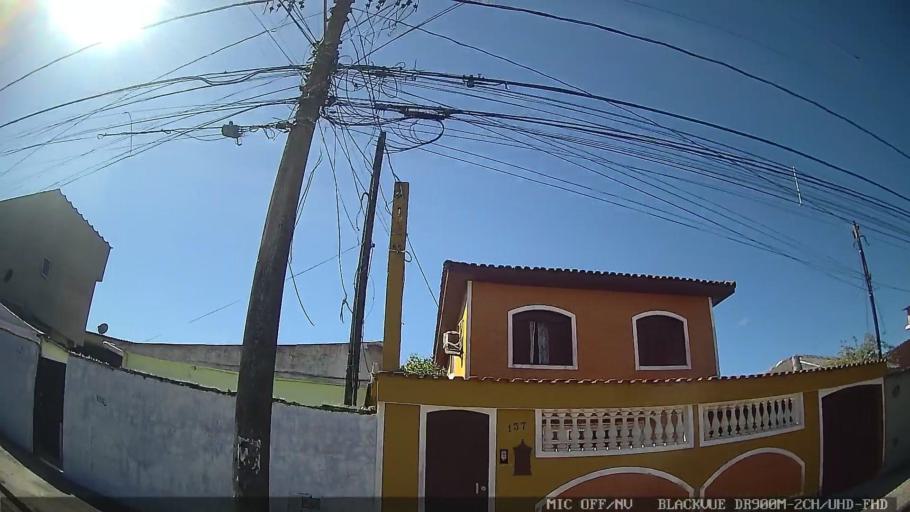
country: BR
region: Sao Paulo
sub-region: Santos
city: Santos
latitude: -23.9404
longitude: -46.2959
